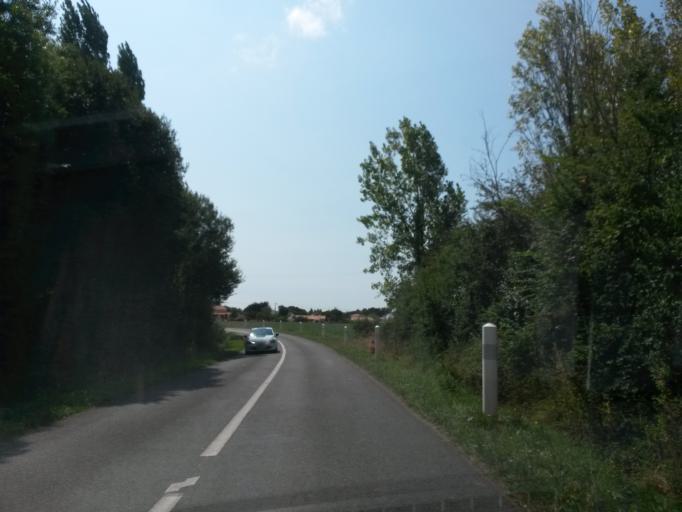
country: FR
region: Pays de la Loire
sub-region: Departement de la Vendee
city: Saint-Hilaire-de-Talmont
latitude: 46.4510
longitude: -1.6243
